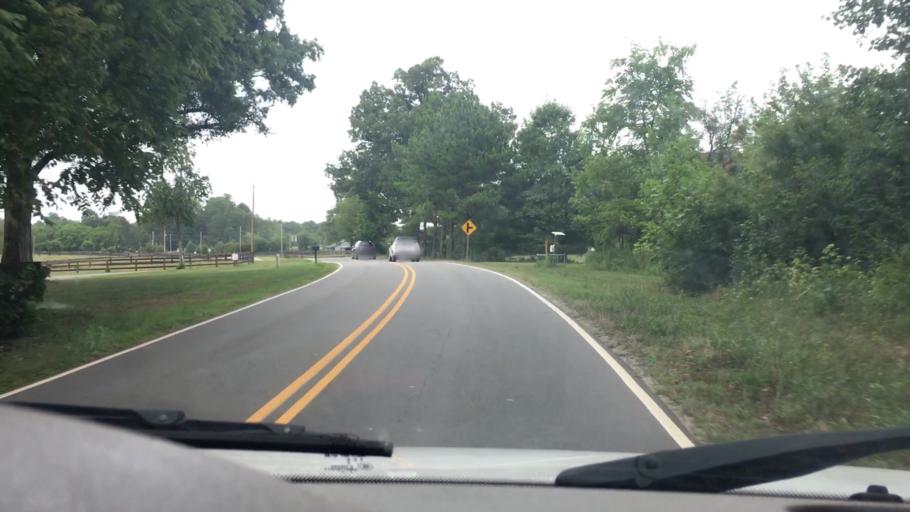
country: US
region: North Carolina
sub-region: Gaston County
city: Davidson
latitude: 35.4579
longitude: -80.7962
